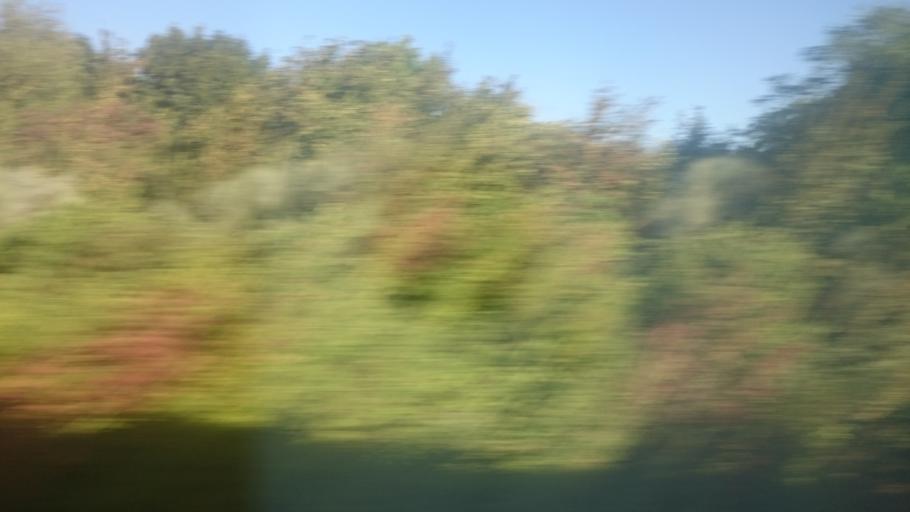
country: FR
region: Centre
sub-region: Departement d'Eure-et-Loir
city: Bonneval
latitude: 48.2077
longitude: 1.4105
